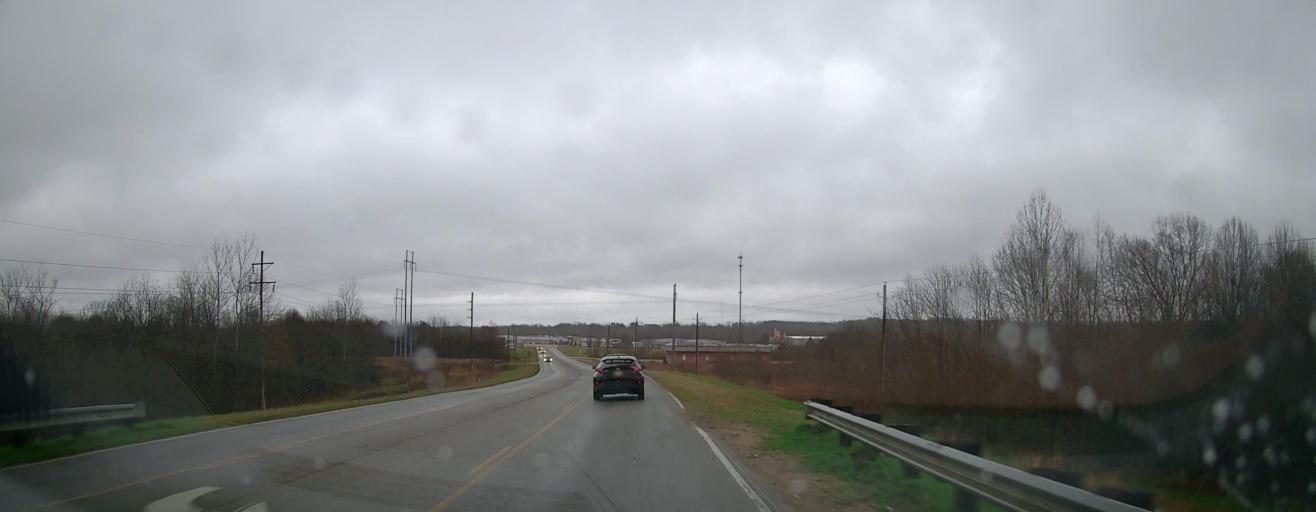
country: US
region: Mississippi
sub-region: Alcorn County
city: Corinth
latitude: 34.9090
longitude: -88.5121
